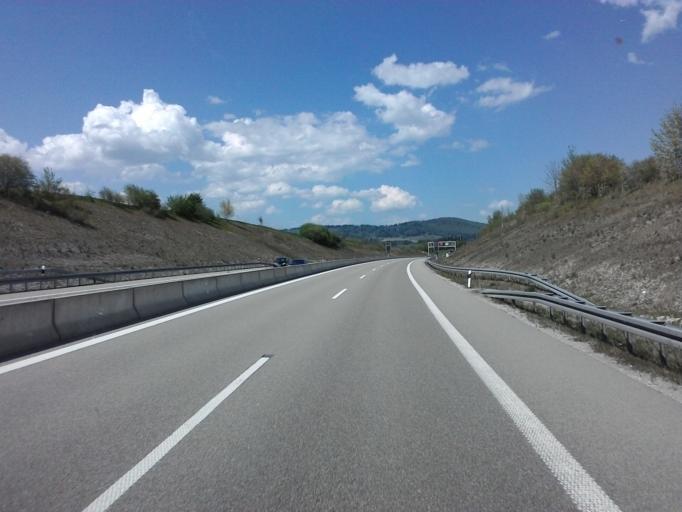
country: DE
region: Bavaria
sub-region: Swabia
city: Hopferau
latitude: 47.5938
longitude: 10.6563
